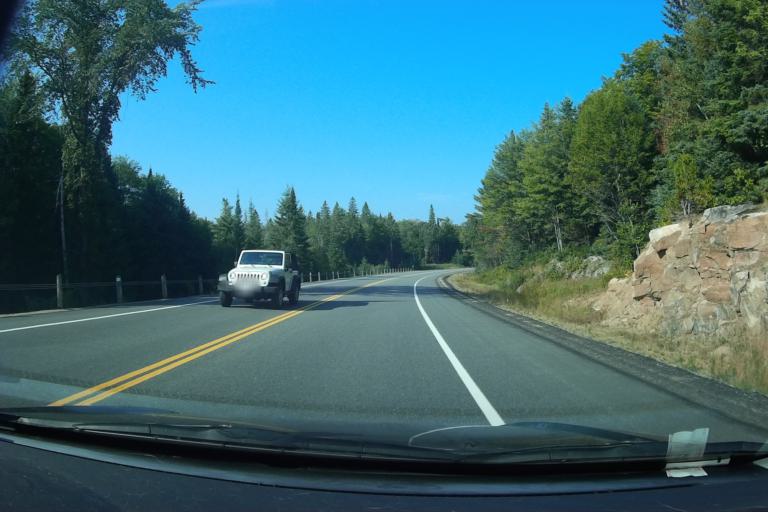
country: CA
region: Ontario
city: Huntsville
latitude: 45.5436
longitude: -78.6570
